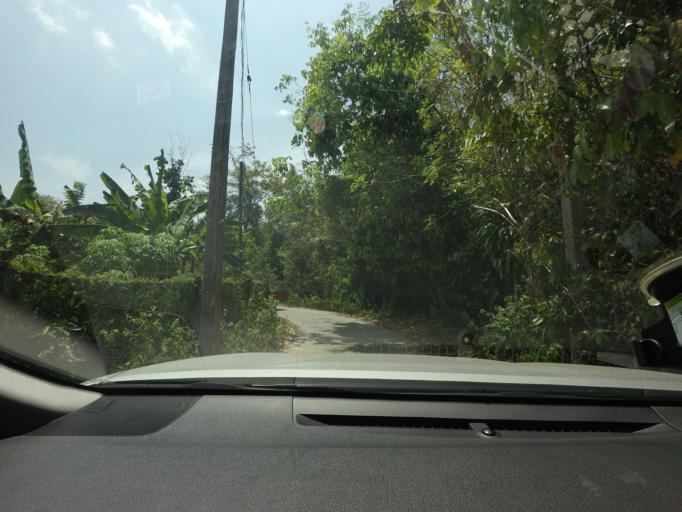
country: TH
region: Narathiwat
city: Rueso
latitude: 6.3881
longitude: 101.5091
